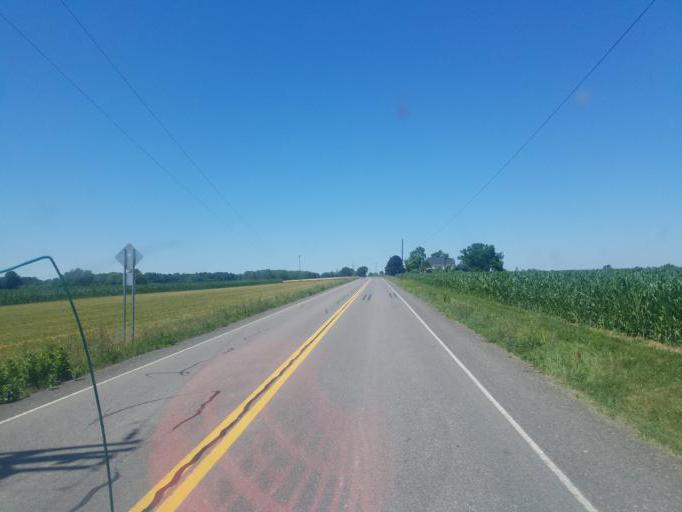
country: US
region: New York
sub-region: Yates County
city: Penn Yan
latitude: 42.6990
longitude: -76.9978
